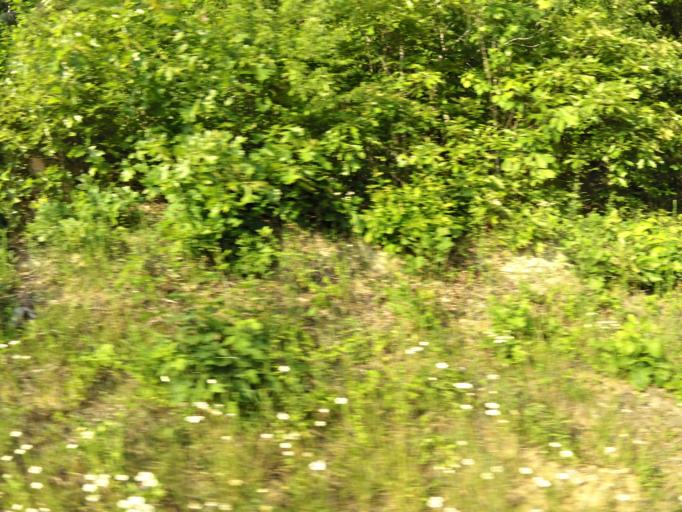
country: US
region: Tennessee
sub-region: Sevier County
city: Sevierville
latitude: 35.8339
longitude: -83.6179
